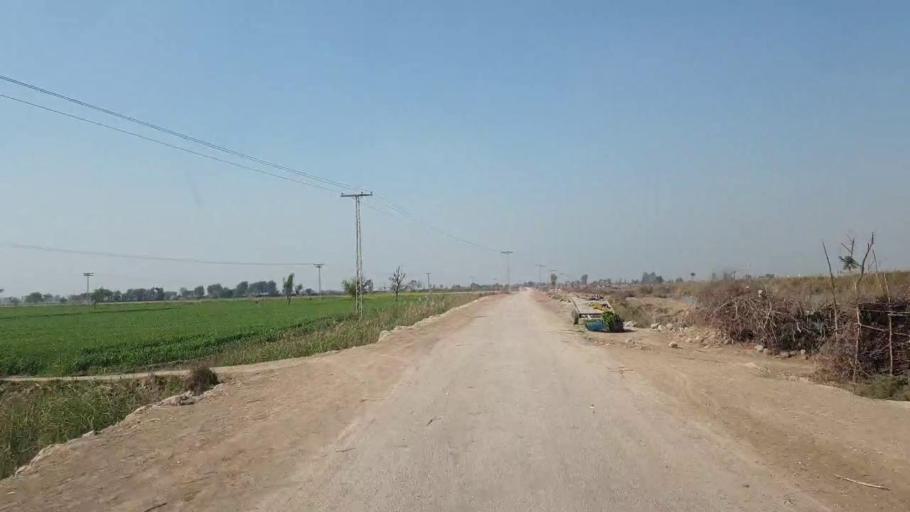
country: PK
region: Sindh
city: Bhit Shah
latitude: 25.9277
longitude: 68.4813
